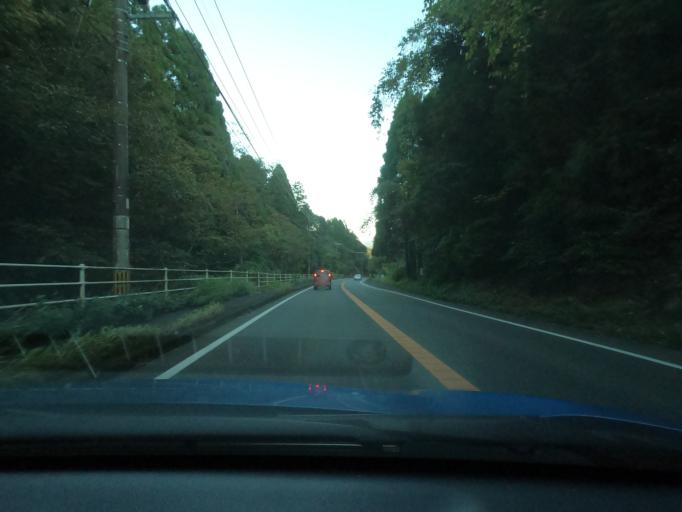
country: JP
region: Kagoshima
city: Satsumasendai
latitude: 31.8112
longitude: 130.3820
